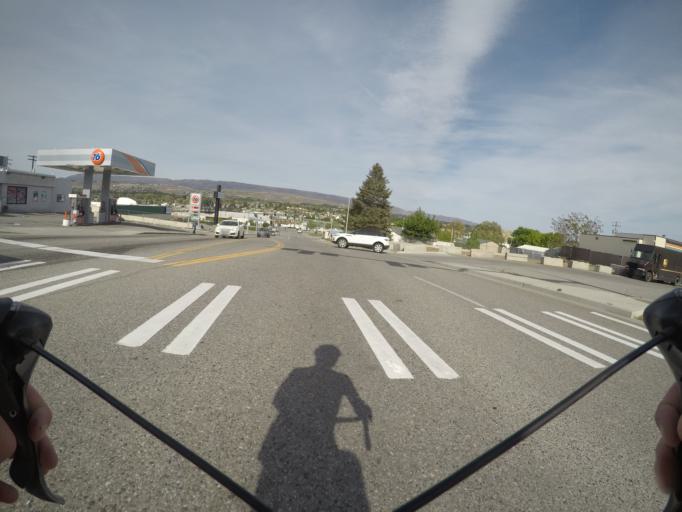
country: US
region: Washington
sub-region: Douglas County
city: East Wenatchee
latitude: 47.4109
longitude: -120.3034
